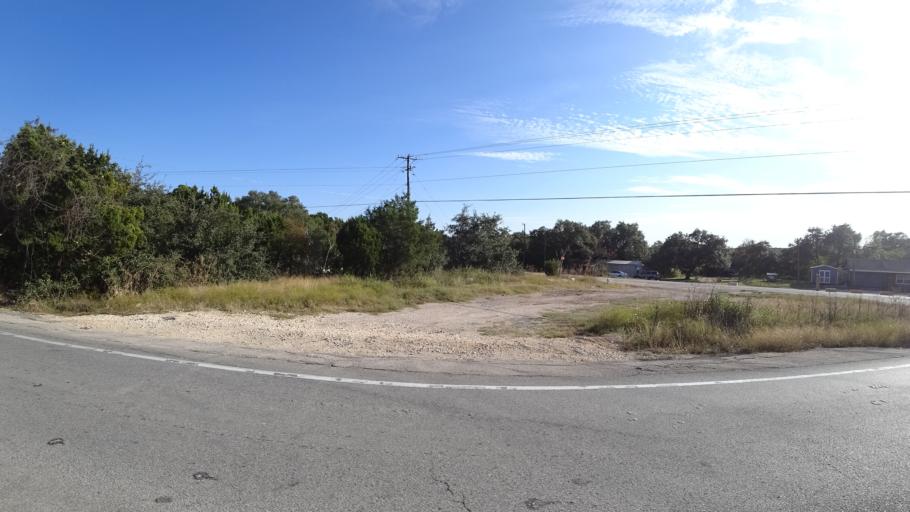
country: US
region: Texas
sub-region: Travis County
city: Bee Cave
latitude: 30.2465
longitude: -97.9267
